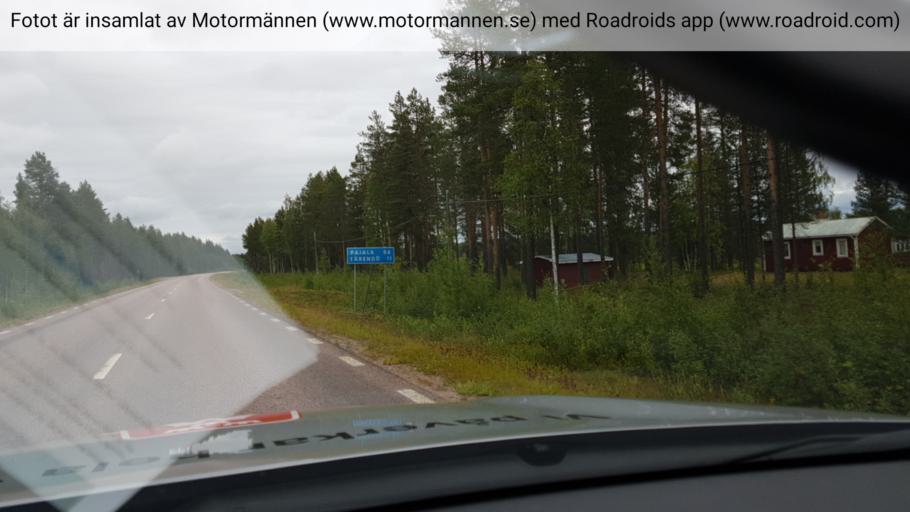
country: SE
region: Norrbotten
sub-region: Overkalix Kommun
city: OEverkalix
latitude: 67.0732
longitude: 22.5255
